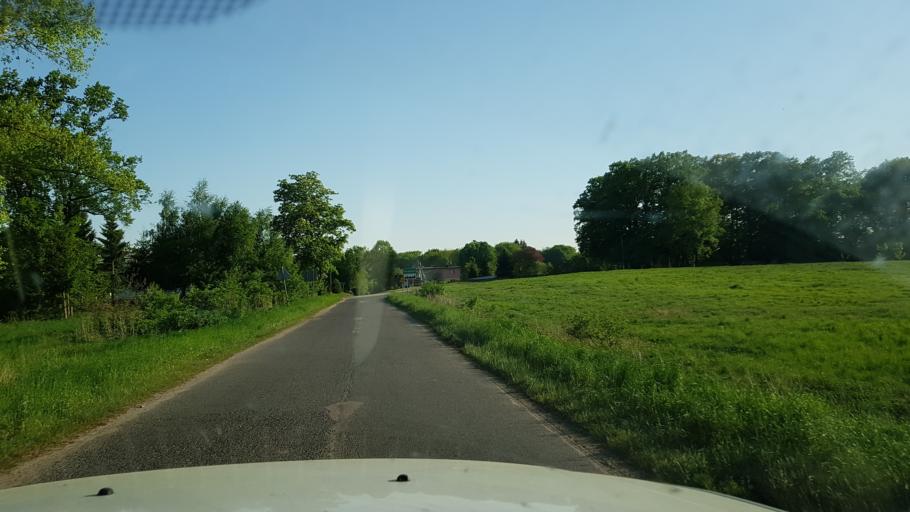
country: PL
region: West Pomeranian Voivodeship
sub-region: Powiat lobeski
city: Radowo Male
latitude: 53.6358
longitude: 15.3755
